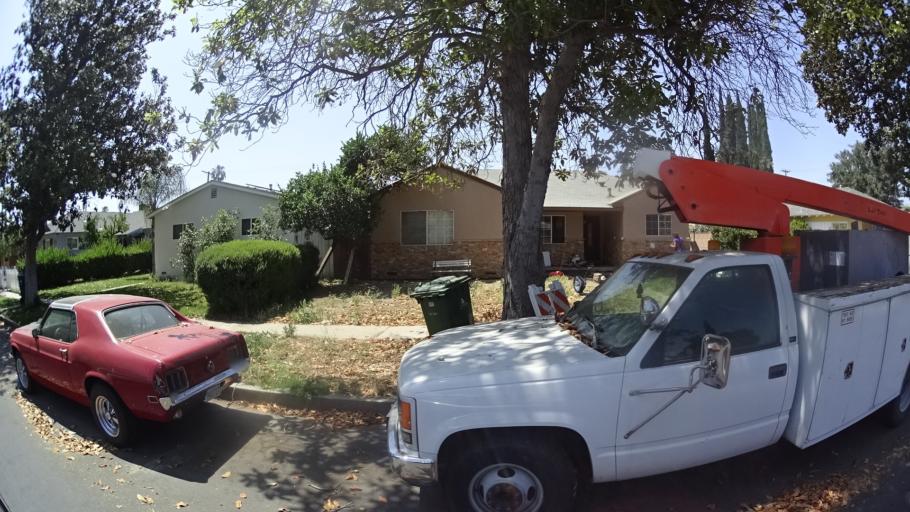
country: US
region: California
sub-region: Los Angeles County
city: Van Nuys
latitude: 34.2093
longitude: -118.4567
